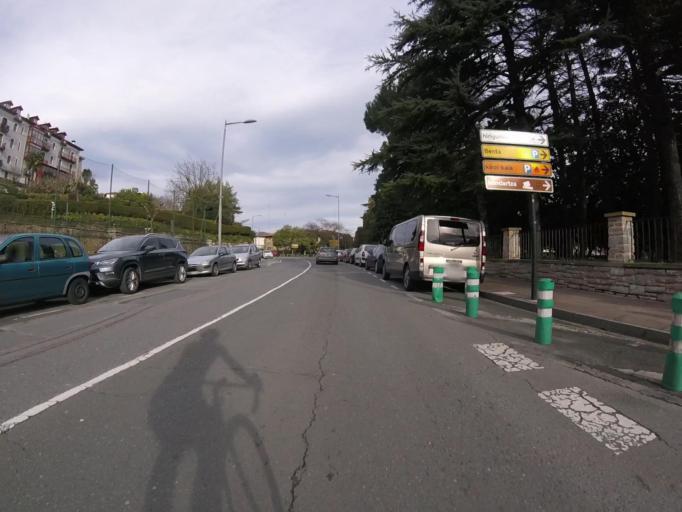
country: ES
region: Basque Country
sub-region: Provincia de Guipuzcoa
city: Fuenterrabia
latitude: 43.3629
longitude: -1.7898
